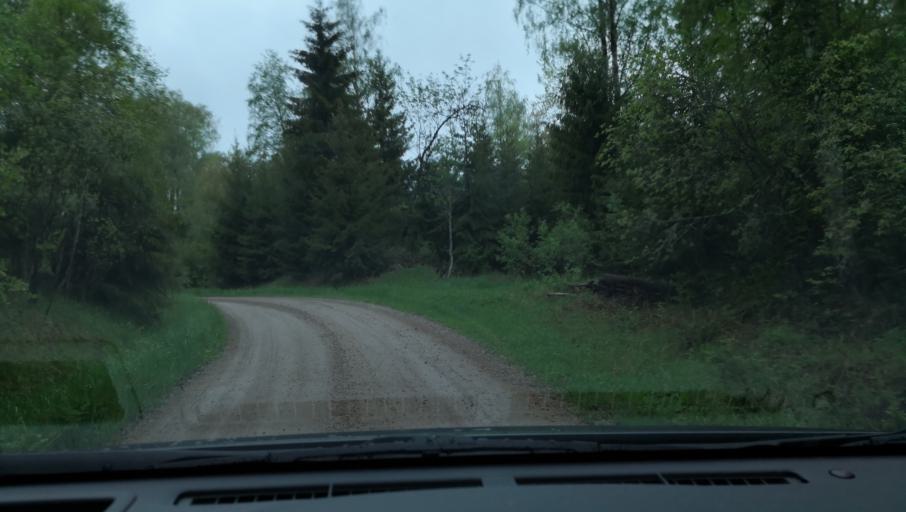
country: SE
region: Uppsala
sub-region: Enkopings Kommun
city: Orsundsbro
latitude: 59.9213
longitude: 17.3430
